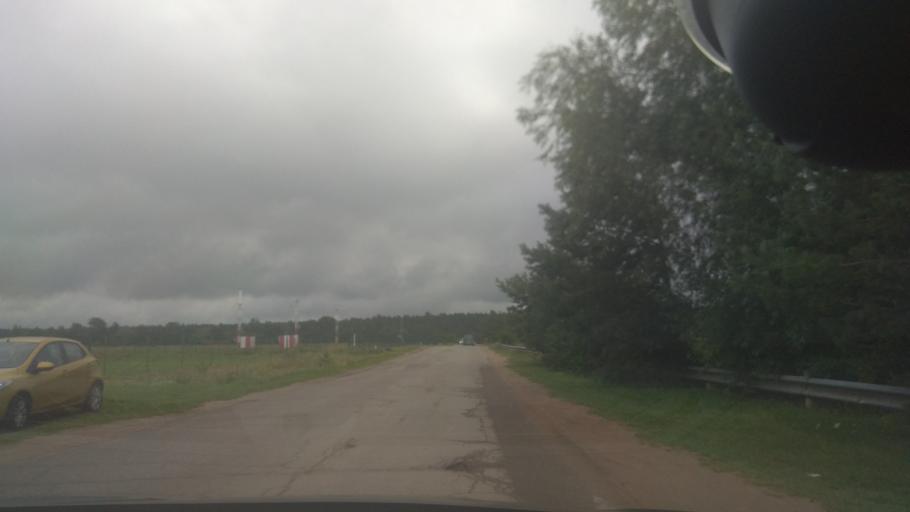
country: LT
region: Klaipedos apskritis
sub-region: Klaipeda
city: Palanga
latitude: 55.9565
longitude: 21.0848
